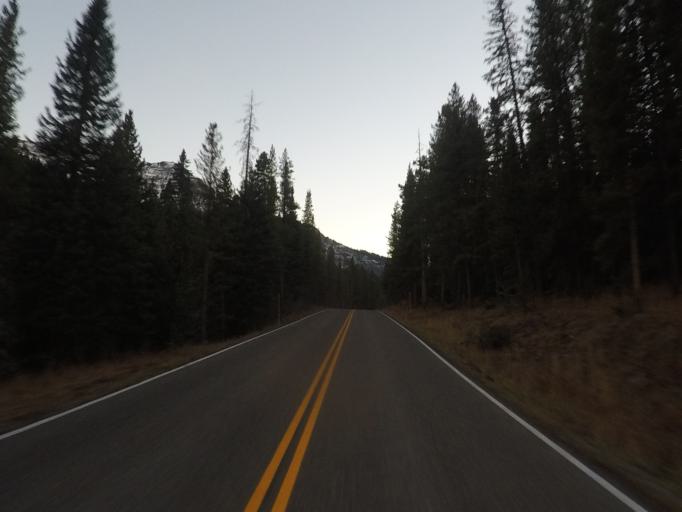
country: US
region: Montana
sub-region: Stillwater County
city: Absarokee
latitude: 44.9332
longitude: -110.0844
